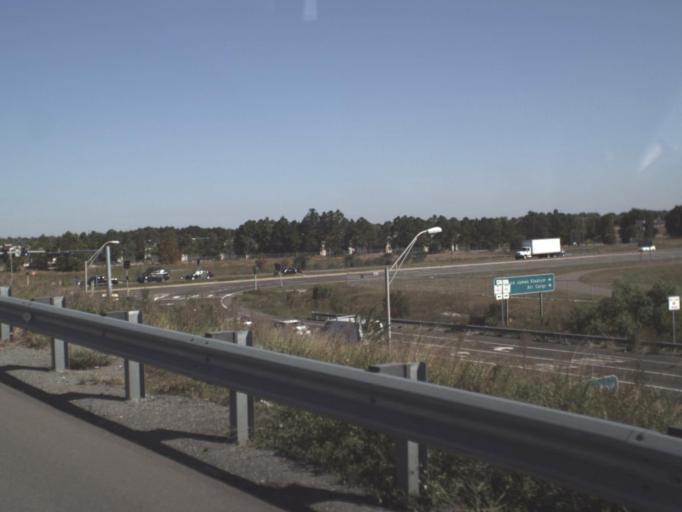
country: US
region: Florida
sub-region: Hillsborough County
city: Town 'n' Country
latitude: 27.9952
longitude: -82.5458
